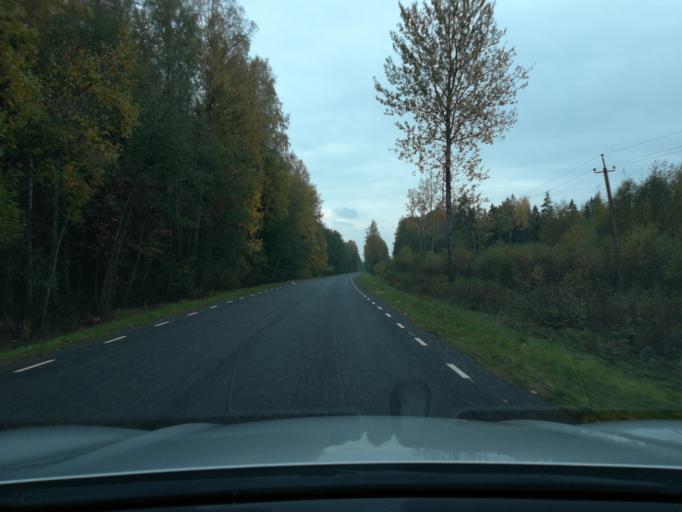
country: EE
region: Ida-Virumaa
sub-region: Johvi vald
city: Johvi
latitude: 59.0441
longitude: 27.3959
